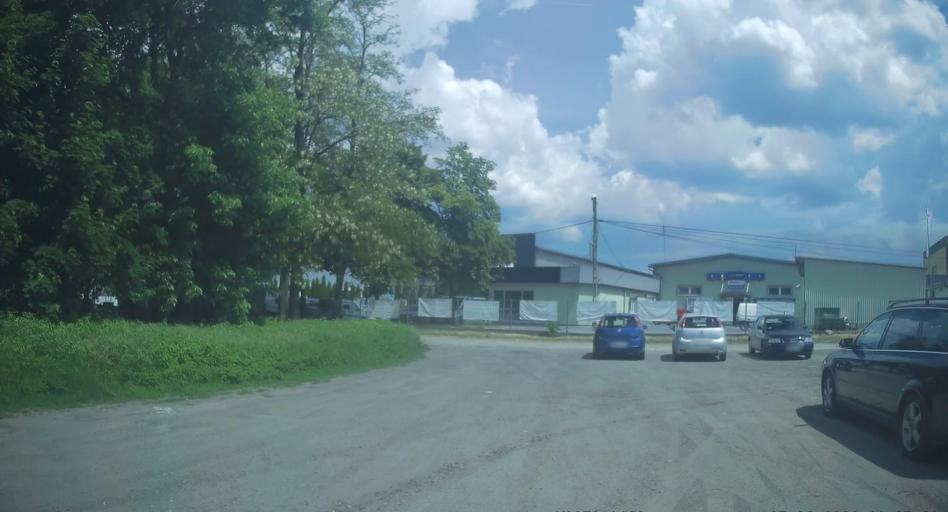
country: PL
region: Subcarpathian Voivodeship
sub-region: Powiat debicki
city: Debica
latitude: 50.0587
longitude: 21.4340
